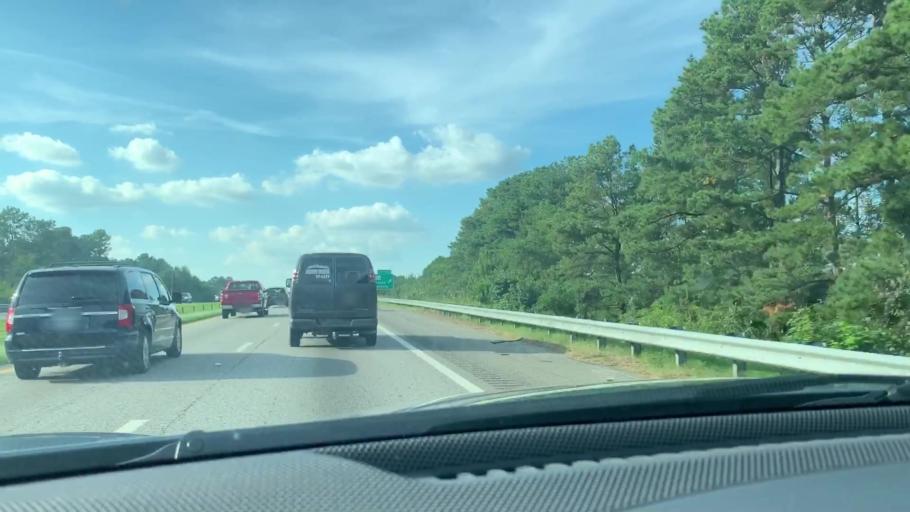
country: US
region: South Carolina
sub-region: Orangeburg County
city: Brookdale
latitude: 33.5178
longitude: -80.7889
